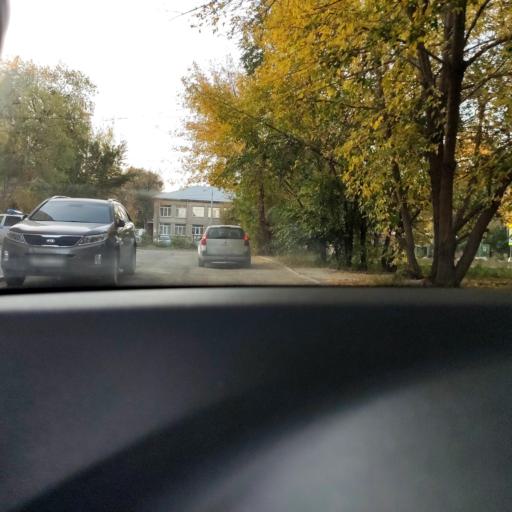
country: RU
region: Samara
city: Samara
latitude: 53.2107
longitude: 50.2555
